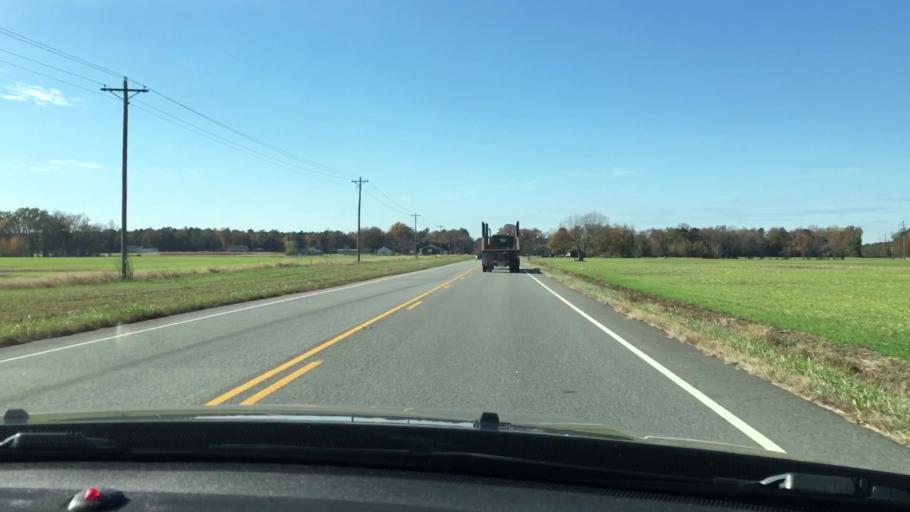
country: US
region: Virginia
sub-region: Hanover County
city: Hanover
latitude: 37.8121
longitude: -77.2937
